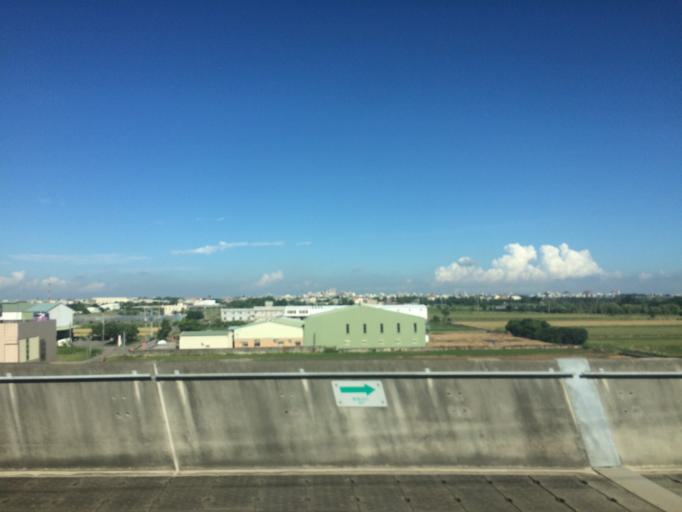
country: TW
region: Taiwan
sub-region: Chiayi
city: Taibao
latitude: 23.5664
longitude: 120.3315
